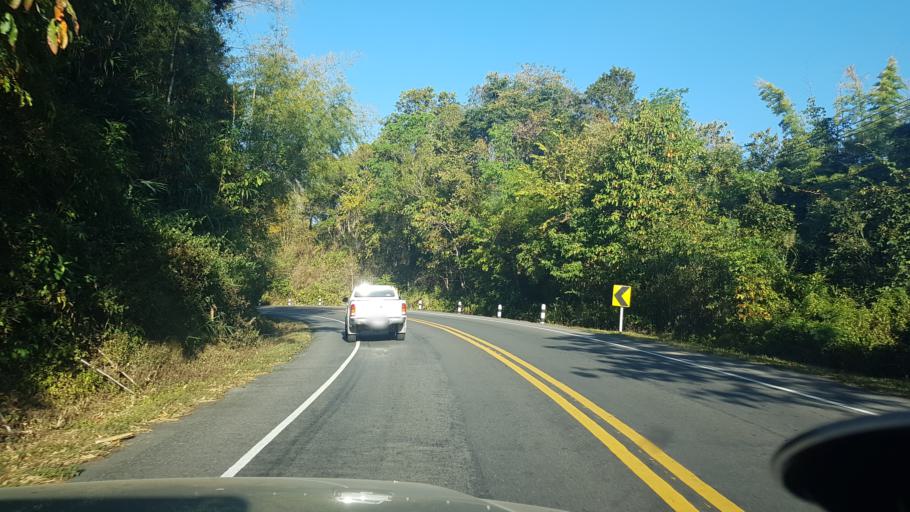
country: TH
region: Phetchabun
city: Nam Nao
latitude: 16.7610
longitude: 101.4812
